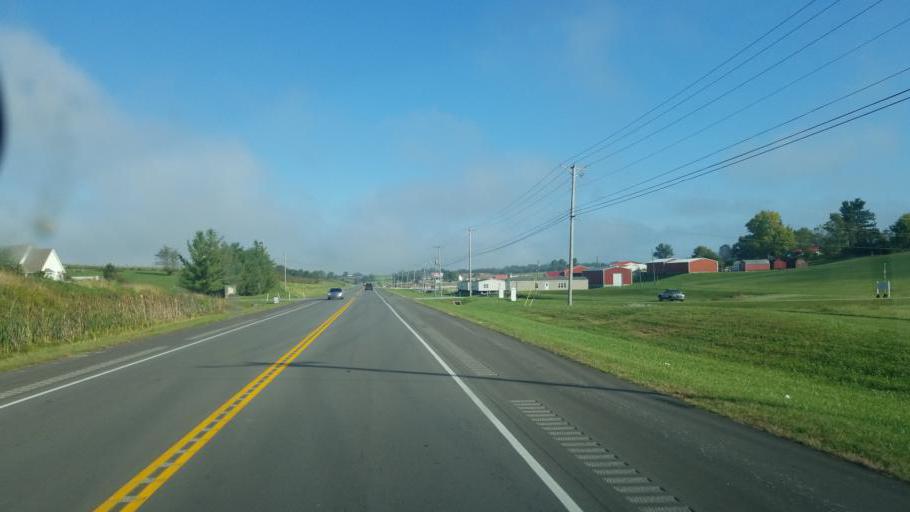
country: US
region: Kentucky
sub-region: Fleming County
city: Flemingsburg
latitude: 38.4684
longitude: -83.7566
